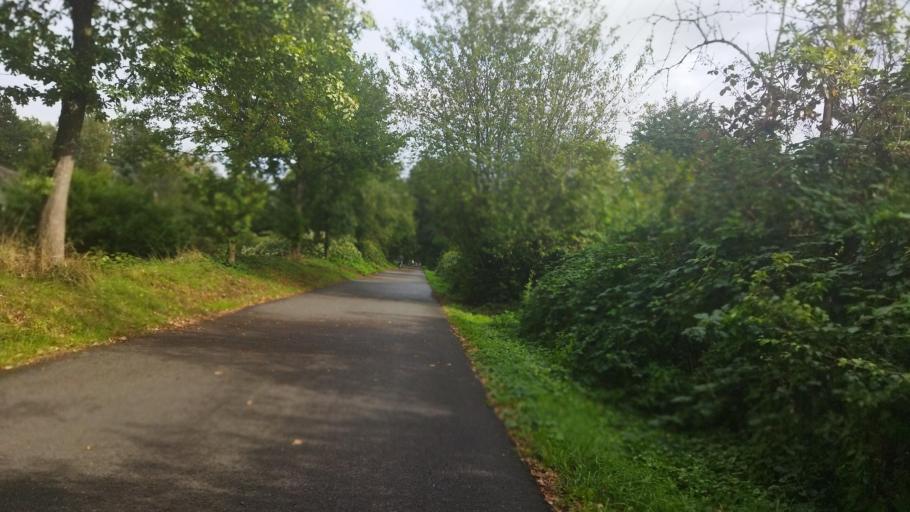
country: DE
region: North Rhine-Westphalia
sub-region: Regierungsbezirk Munster
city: Gelsenkirchen
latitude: 51.4844
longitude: 7.1052
